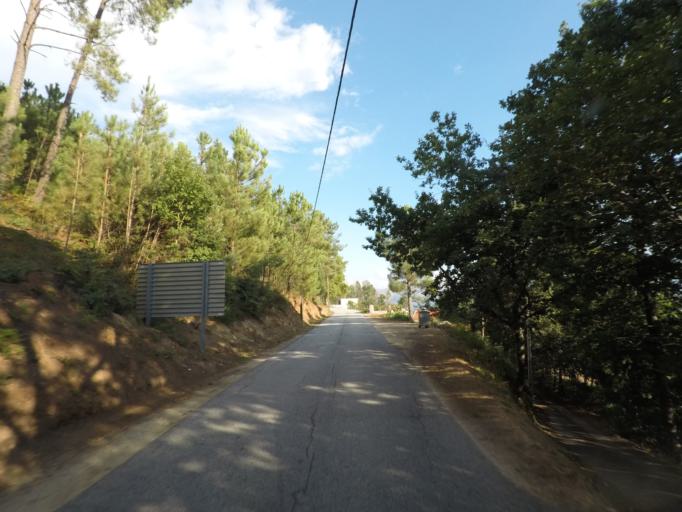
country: PT
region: Porto
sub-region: Baiao
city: Valadares
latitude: 41.1784
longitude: -7.9388
